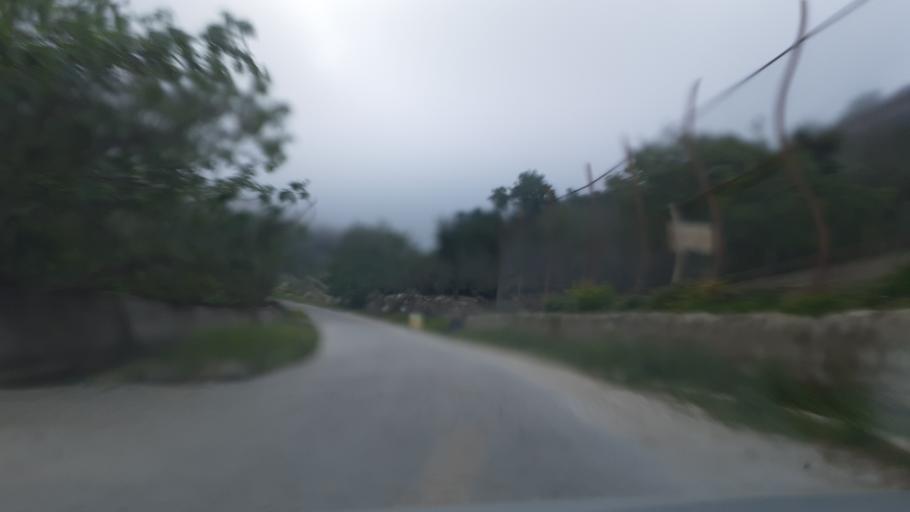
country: TR
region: Hatay
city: Yeditepe
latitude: 35.9678
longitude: 36.0100
